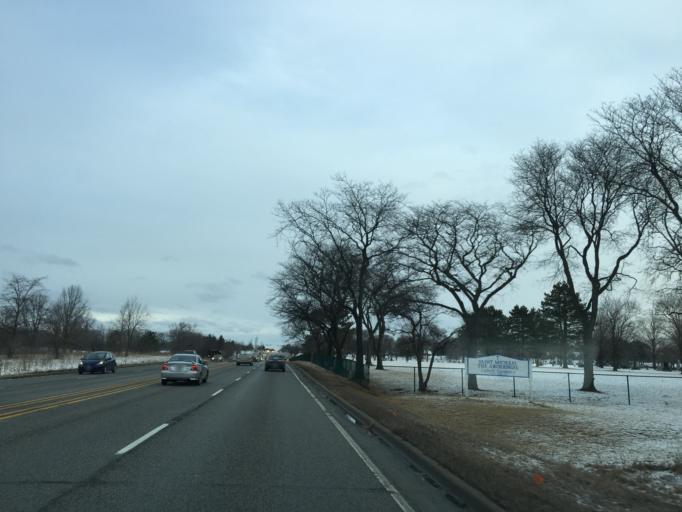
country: US
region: Illinois
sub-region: Cook County
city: Hoffman Estates
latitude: 42.0733
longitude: -88.0779
